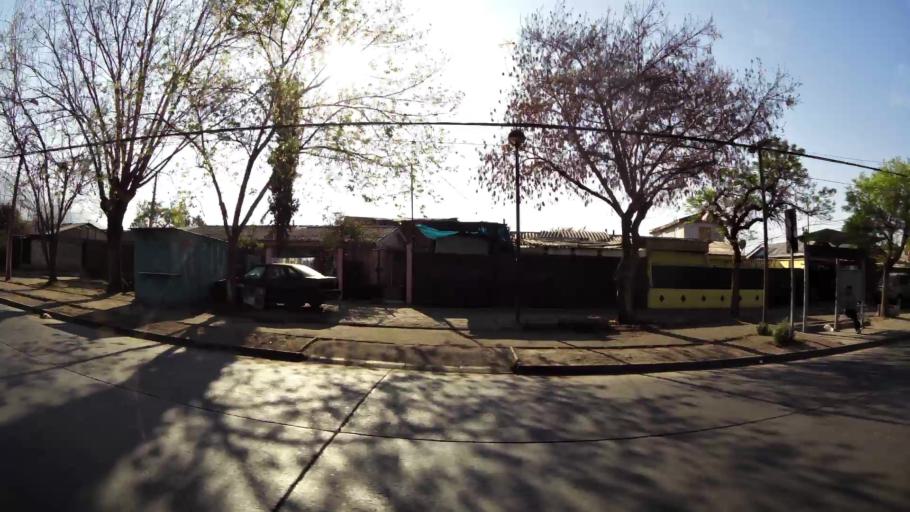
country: CL
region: Santiago Metropolitan
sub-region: Provincia de Santiago
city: Santiago
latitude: -33.3813
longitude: -70.6575
